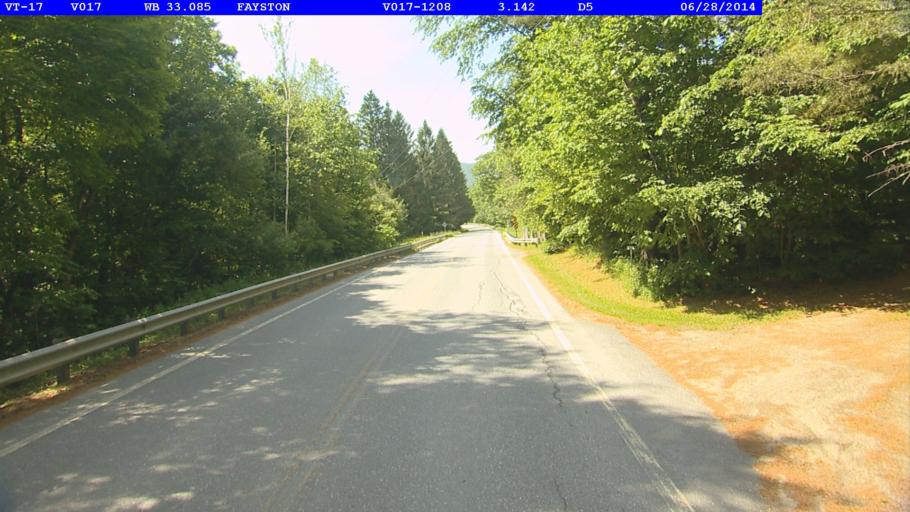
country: US
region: Vermont
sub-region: Washington County
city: Waterbury
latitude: 44.1937
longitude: -72.8895
